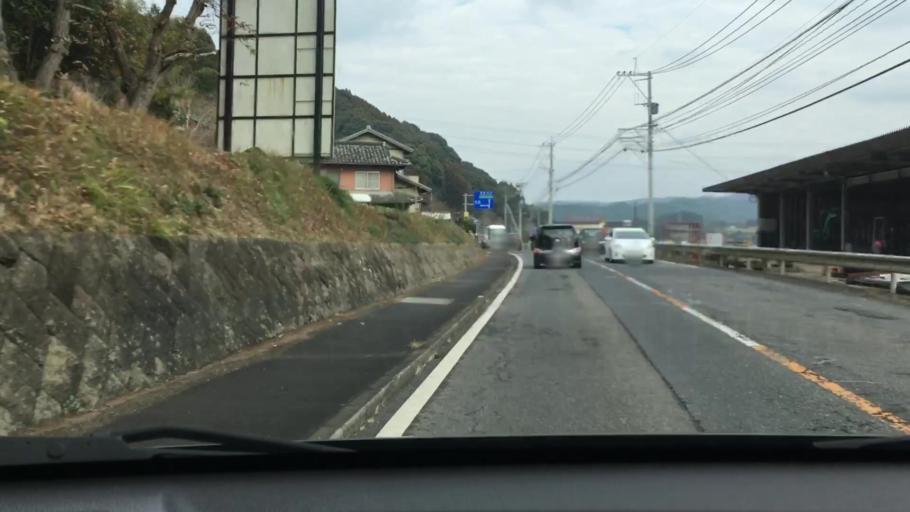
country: JP
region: Saga Prefecture
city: Imaricho-ko
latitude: 33.3027
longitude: 129.9209
